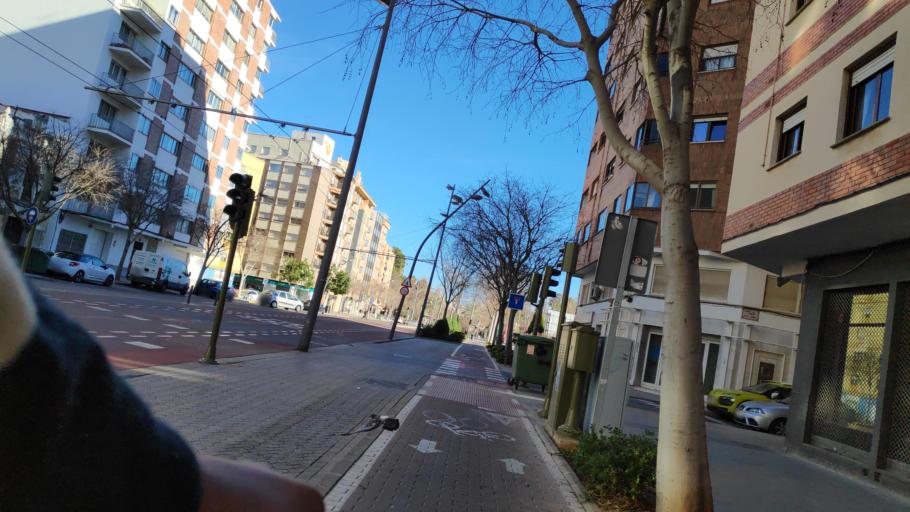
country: ES
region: Valencia
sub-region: Provincia de Castello
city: Castello de la Plana
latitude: 39.9891
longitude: -0.0487
